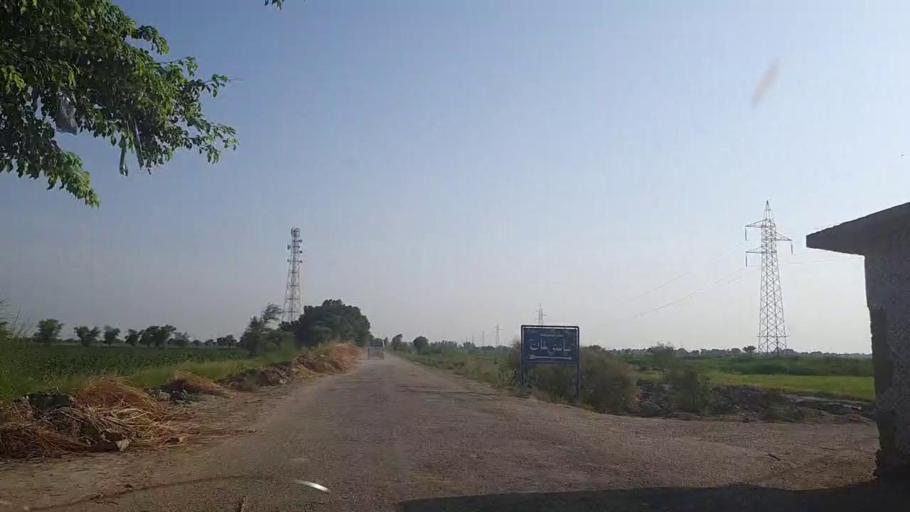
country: PK
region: Sindh
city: Khanpur
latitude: 27.7294
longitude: 69.3043
